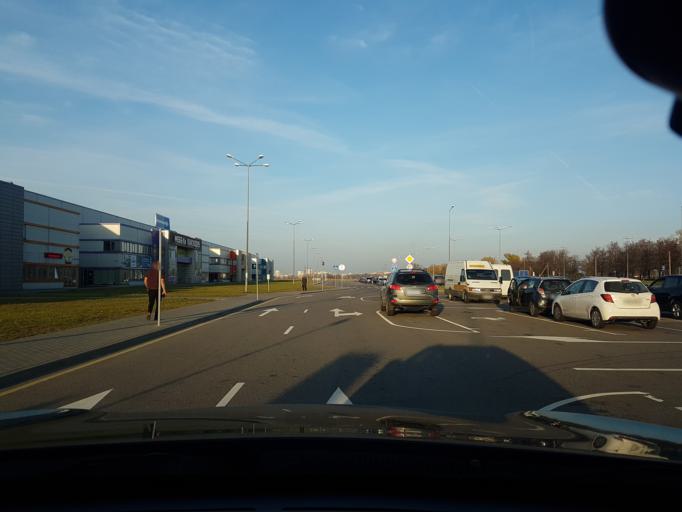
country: BY
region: Minsk
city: Shchomyslitsa
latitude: 53.8222
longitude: 27.4366
